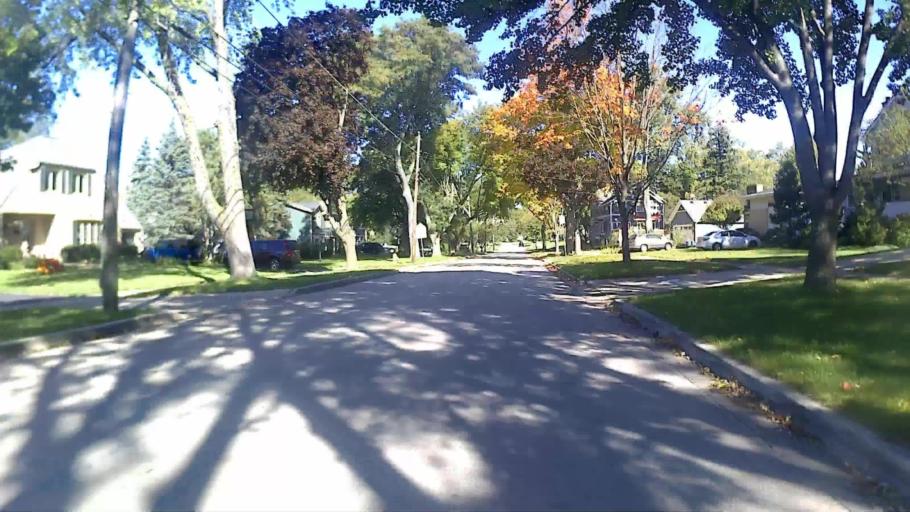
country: US
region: Illinois
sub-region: DuPage County
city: Glen Ellyn
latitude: 41.8673
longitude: -88.0716
